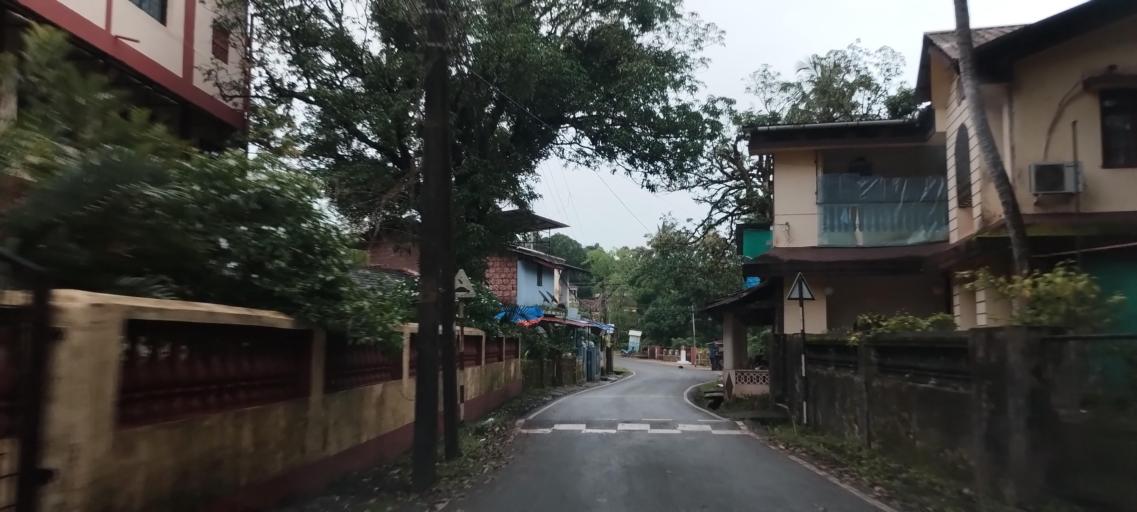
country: IN
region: Goa
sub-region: North Goa
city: Jua
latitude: 15.5272
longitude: 73.9033
